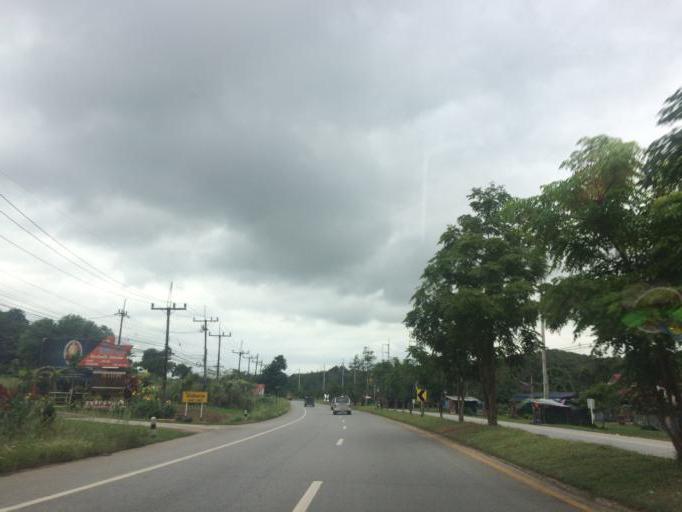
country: TH
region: Chiang Rai
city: Mae Chan
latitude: 20.1236
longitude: 99.8680
